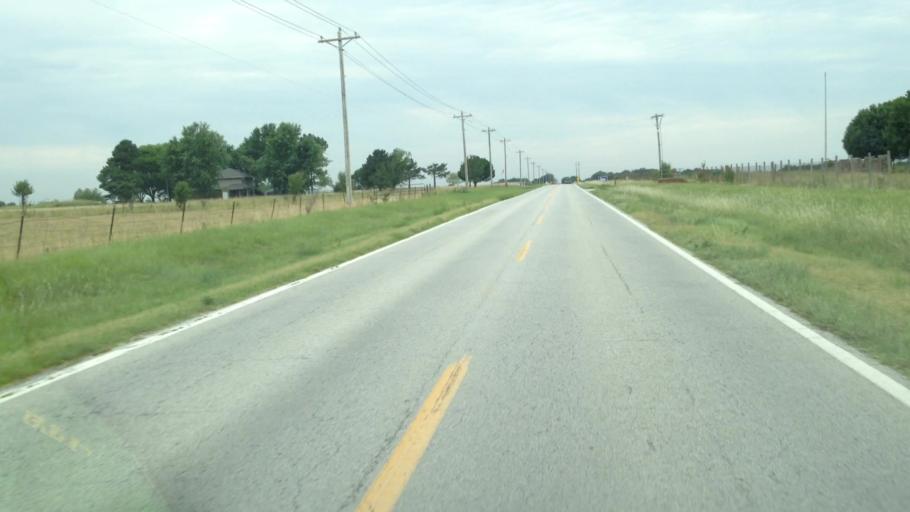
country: US
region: Oklahoma
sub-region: Delaware County
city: Cleora
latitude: 36.6126
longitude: -94.9738
